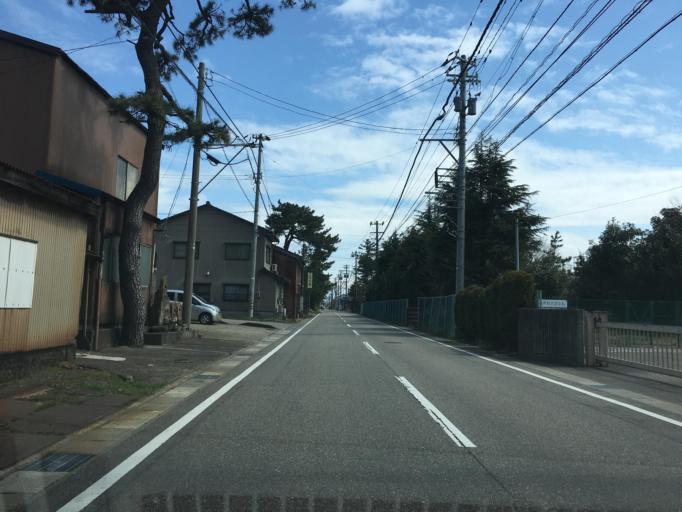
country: JP
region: Toyama
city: Nishishinminato
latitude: 36.7778
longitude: 137.1018
